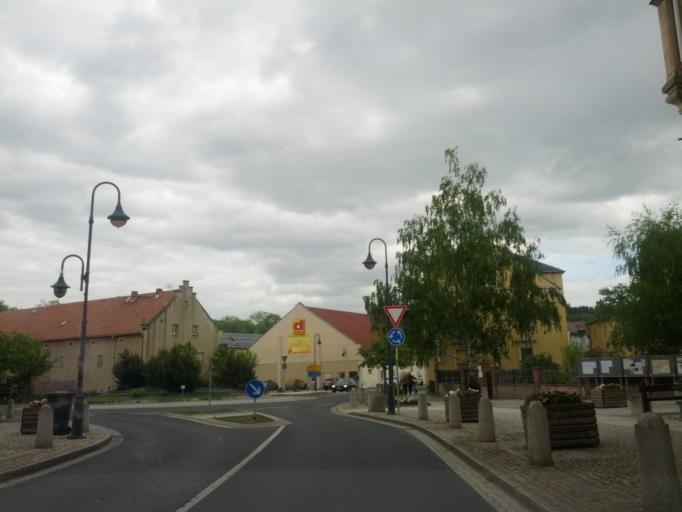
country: DE
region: Saxony
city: Kreischa
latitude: 50.9453
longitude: 13.7594
